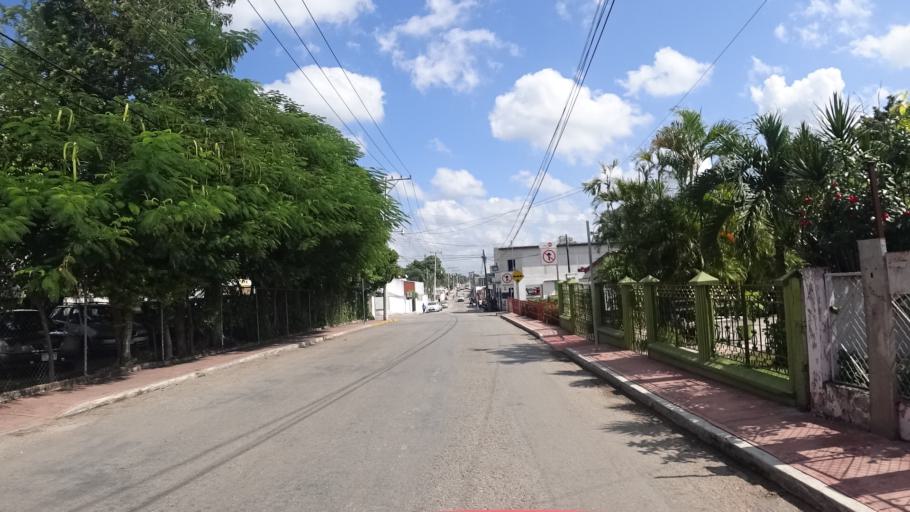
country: MX
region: Yucatan
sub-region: Tizimin
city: Tizimin
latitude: 21.1345
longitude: -88.1535
